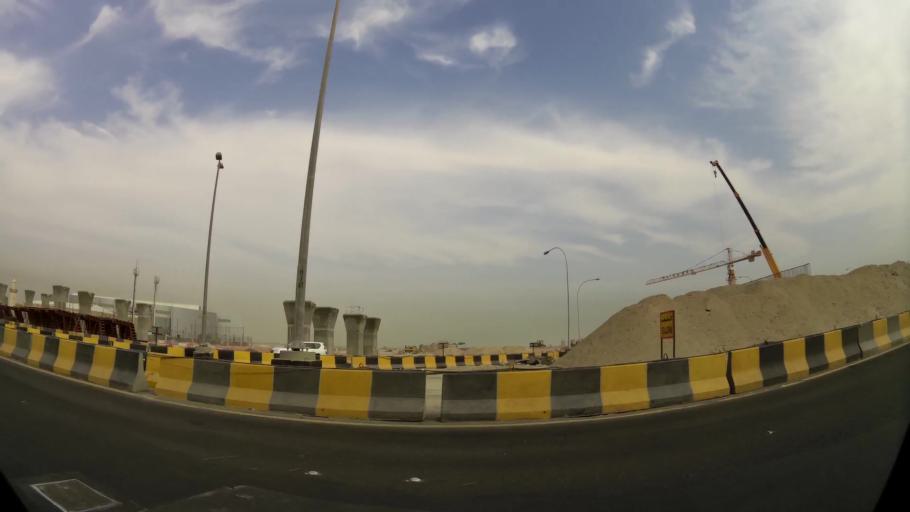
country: KW
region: Al Asimah
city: Ar Rabiyah
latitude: 29.3195
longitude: 47.8305
